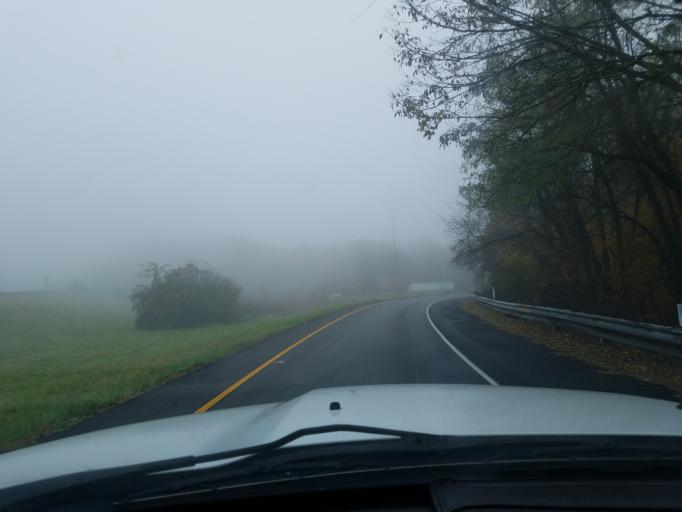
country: US
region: Indiana
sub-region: Floyd County
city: Galena
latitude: 38.3046
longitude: -85.8919
